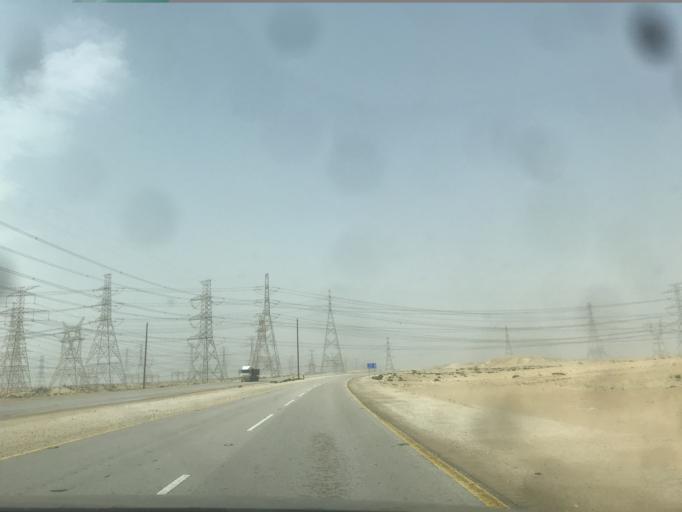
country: SA
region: Eastern Province
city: Abqaiq
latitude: 25.9060
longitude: 49.9146
